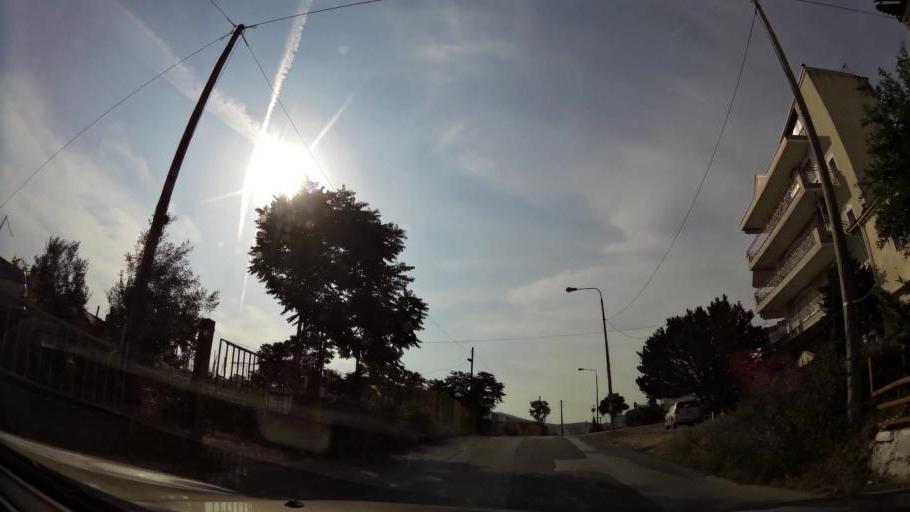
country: GR
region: Central Macedonia
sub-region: Nomos Thessalonikis
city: Sykies
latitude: 40.6563
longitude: 22.9516
